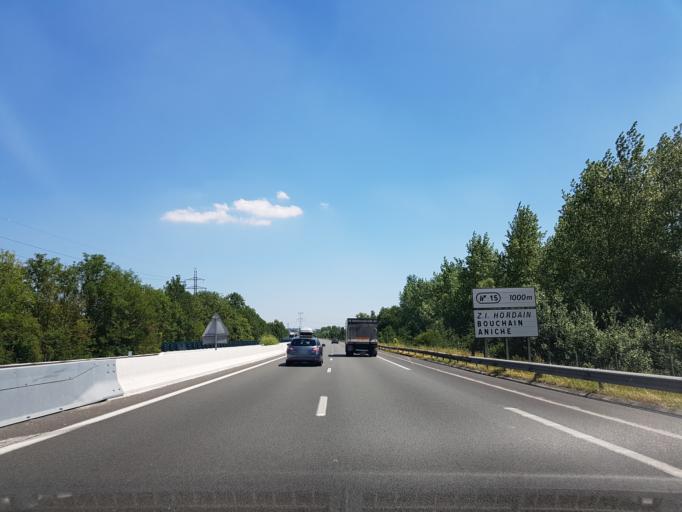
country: FR
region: Nord-Pas-de-Calais
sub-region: Departement du Nord
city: Iwuy
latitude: 50.2446
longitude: 3.3060
